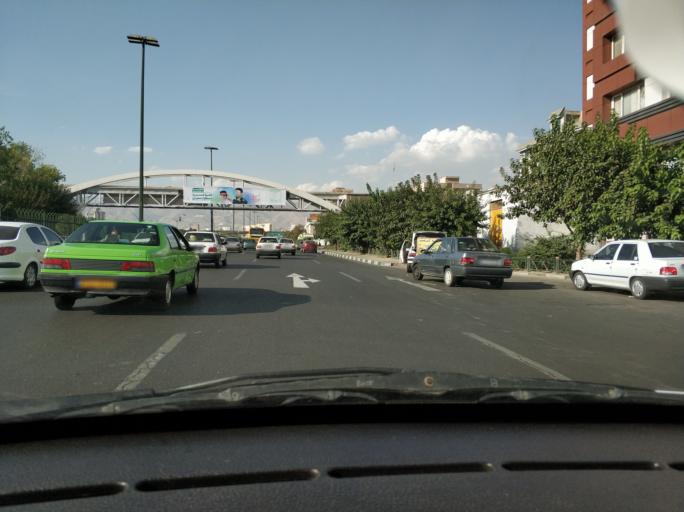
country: IR
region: Tehran
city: Tehran
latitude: 35.7051
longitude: 51.3375
